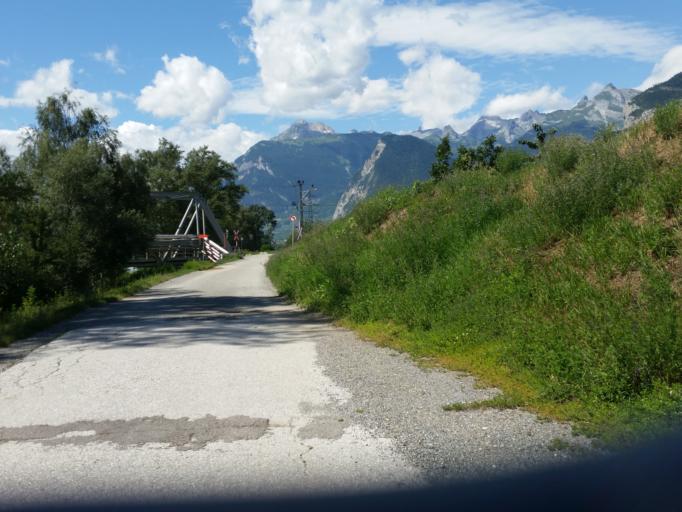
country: CH
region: Valais
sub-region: Conthey District
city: Vetroz
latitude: 46.2008
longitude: 7.2885
